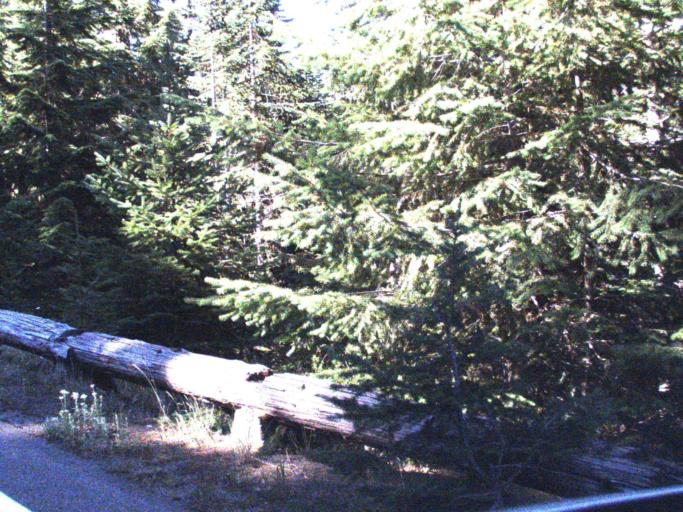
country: US
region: Washington
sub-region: King County
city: Enumclaw
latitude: 46.8934
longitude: -121.5442
